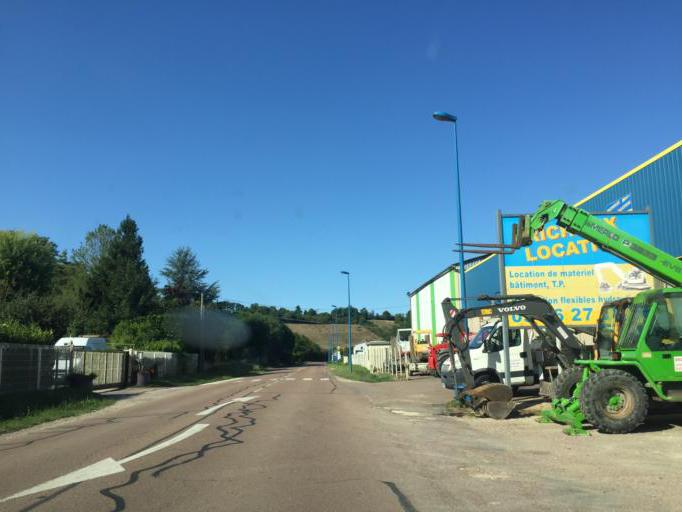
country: FR
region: Bourgogne
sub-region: Departement de la Nievre
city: Clamecy
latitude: 47.4526
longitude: 3.5022
